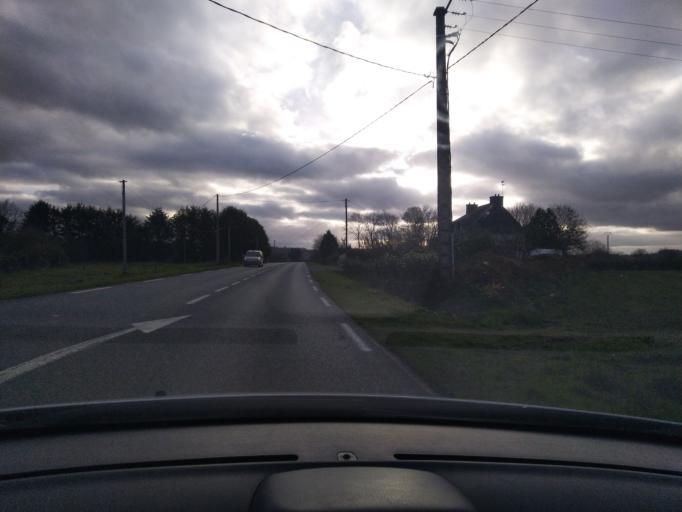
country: FR
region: Brittany
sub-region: Departement des Cotes-d'Armor
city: Plouaret
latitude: 48.5956
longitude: -3.4930
